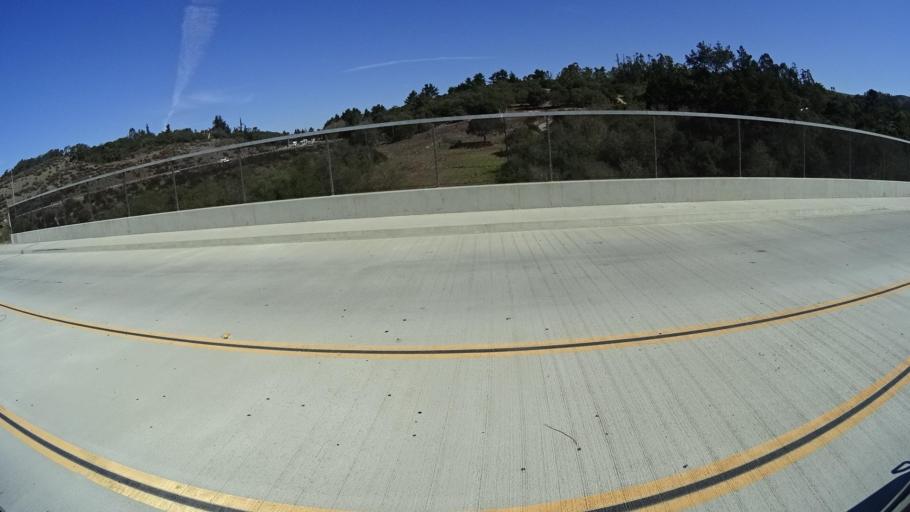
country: US
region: California
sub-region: Monterey County
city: Prunedale
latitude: 36.8171
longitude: -121.6318
